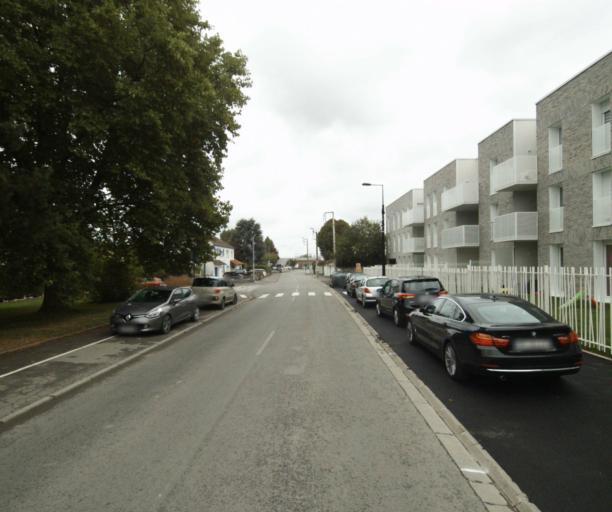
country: FR
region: Nord-Pas-de-Calais
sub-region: Departement du Nord
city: Ronchin
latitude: 50.5876
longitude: 3.0852
